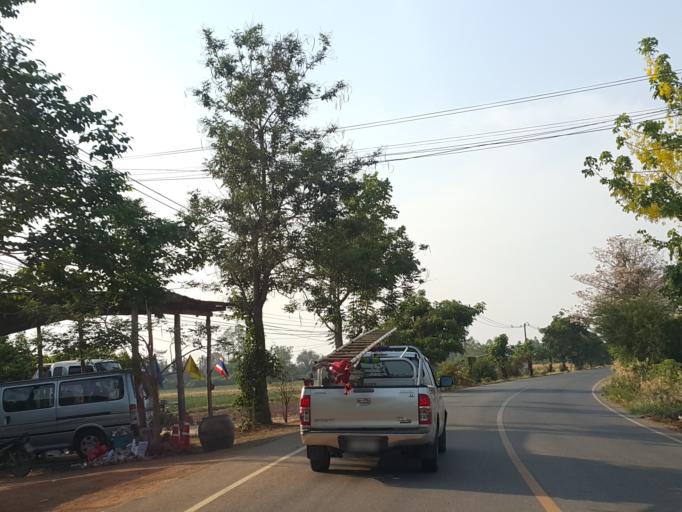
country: TH
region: Phitsanulok
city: Phrom Phiram
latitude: 17.1283
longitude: 100.1529
